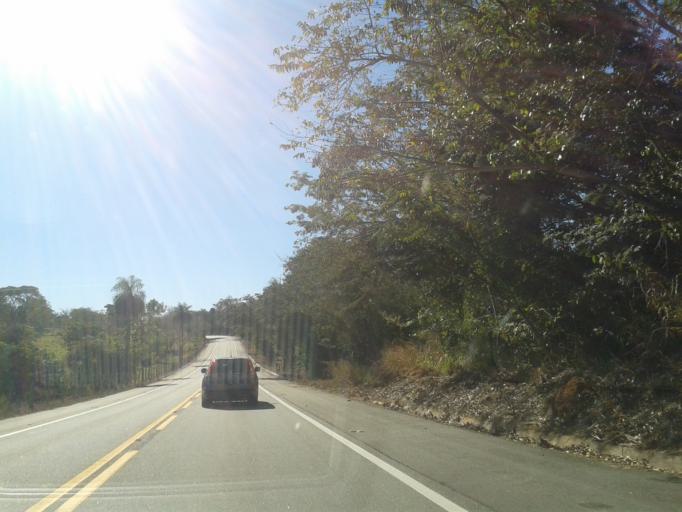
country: BR
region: Goias
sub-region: Itapuranga
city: Itapuranga
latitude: -15.5905
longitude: -50.2598
